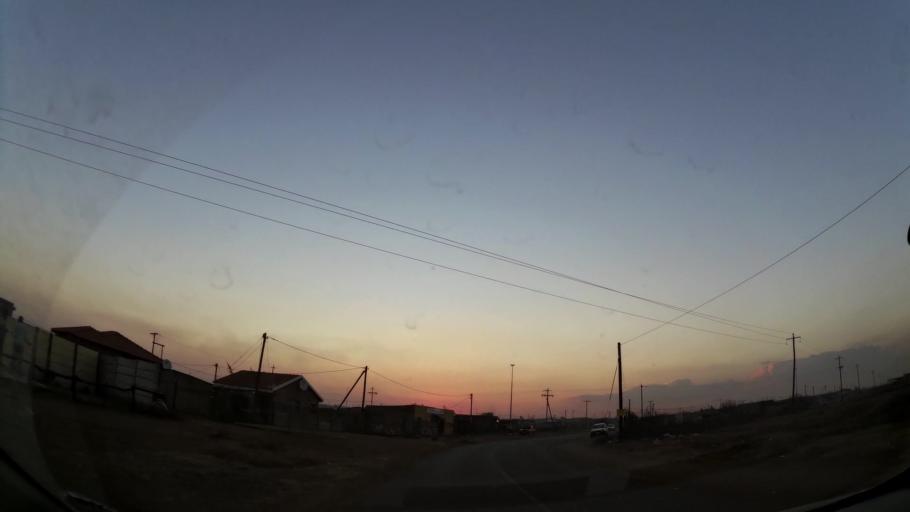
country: ZA
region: Gauteng
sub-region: Ekurhuleni Metropolitan Municipality
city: Nigel
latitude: -26.3676
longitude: 28.3944
